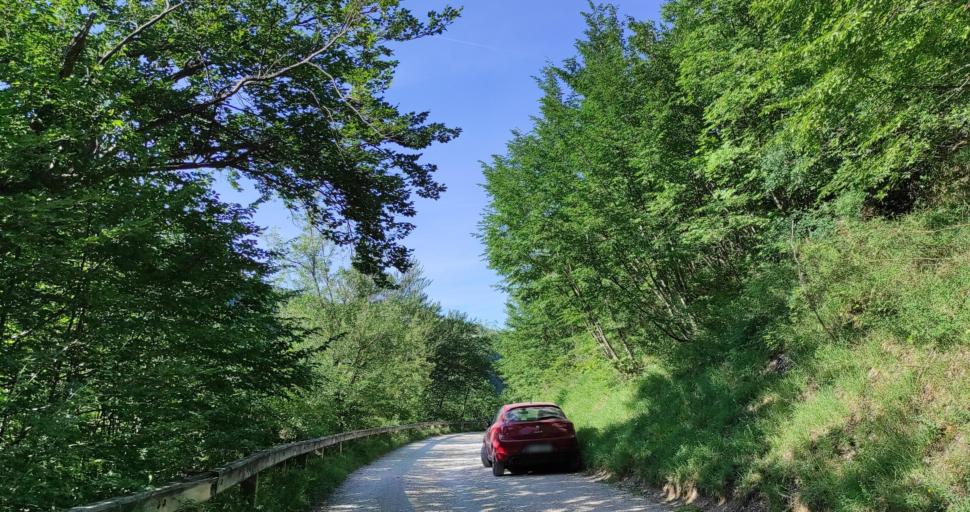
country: IT
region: The Marches
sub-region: Provincia di Ascoli Piceno
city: Montemonaco
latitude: 42.9290
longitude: 13.2889
